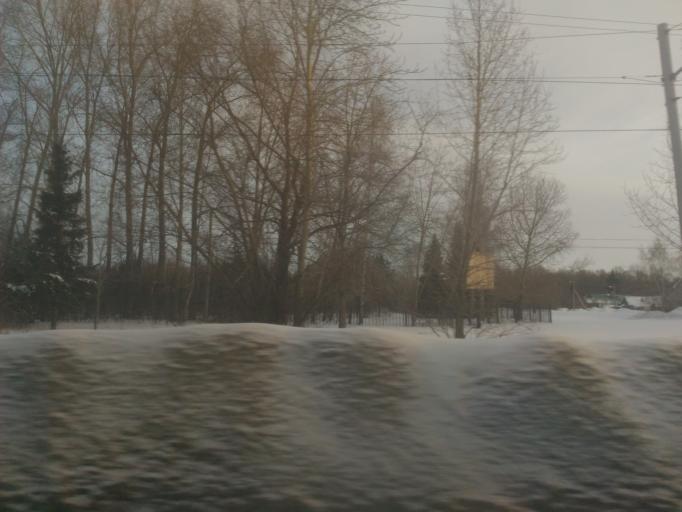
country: RU
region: Ulyanovsk
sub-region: Ulyanovskiy Rayon
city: Ulyanovsk
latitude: 54.3615
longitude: 48.3408
